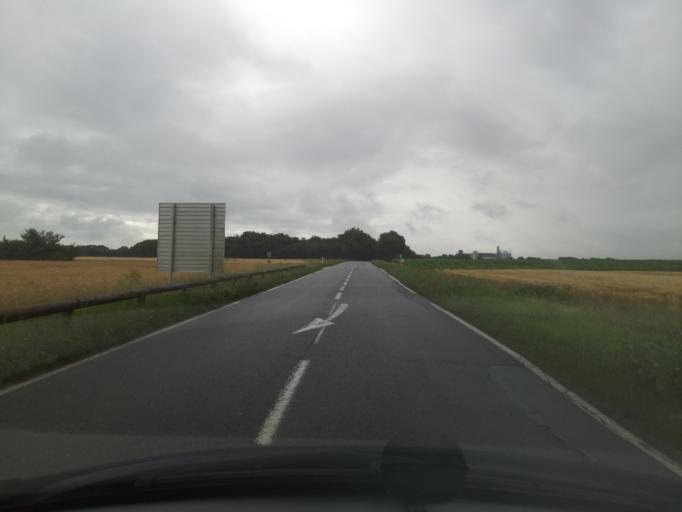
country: FR
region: Poitou-Charentes
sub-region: Departement de la Charente-Maritime
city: Courcon
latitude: 46.1819
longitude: -0.8543
